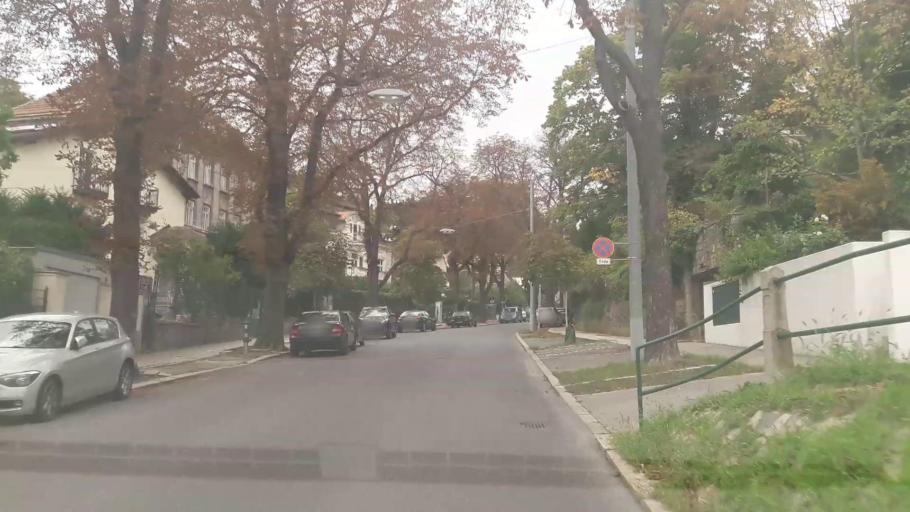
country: AT
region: Lower Austria
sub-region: Politischer Bezirk Korneuburg
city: Langenzersdorf
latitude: 48.2601
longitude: 16.3343
